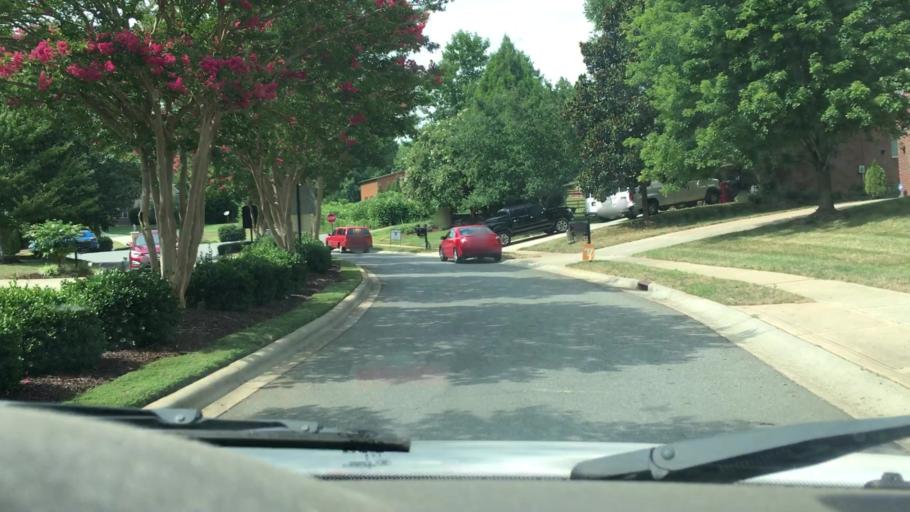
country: US
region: North Carolina
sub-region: Gaston County
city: Davidson
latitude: 35.4718
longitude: -80.7872
